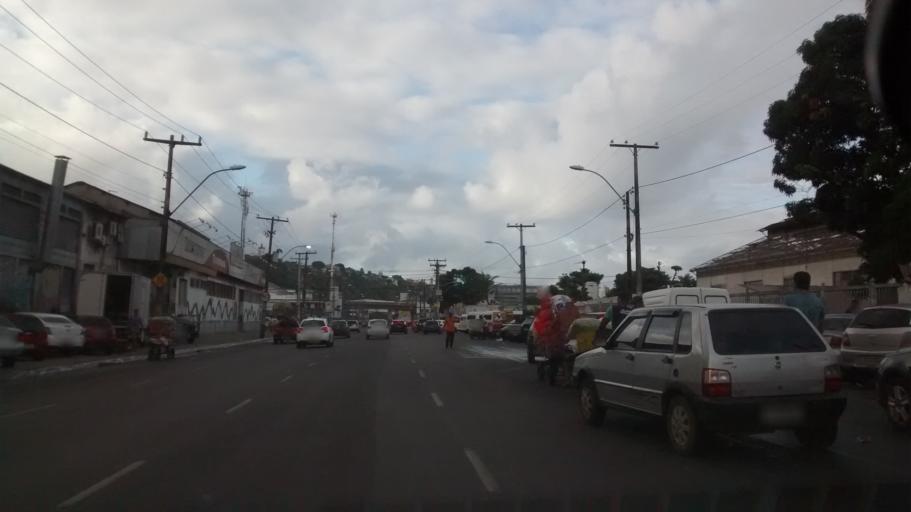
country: BR
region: Bahia
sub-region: Salvador
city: Salvador
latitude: -12.9538
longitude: -38.5018
